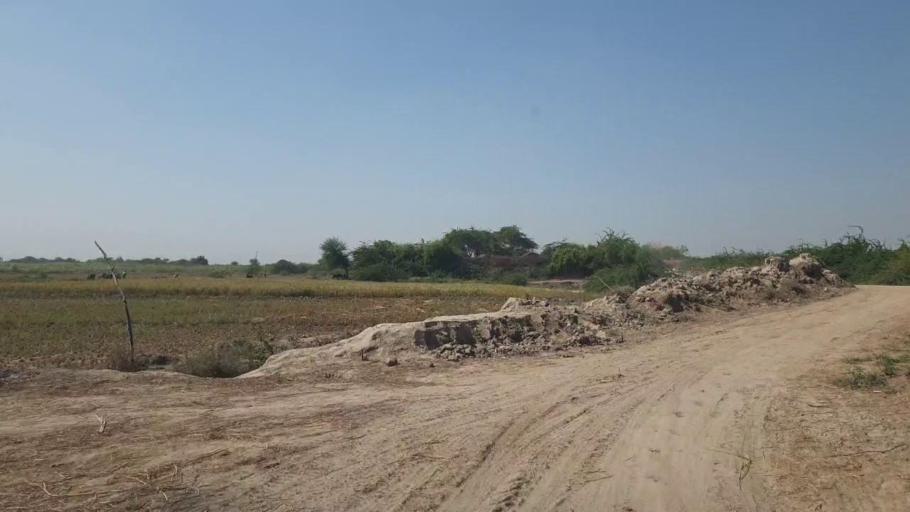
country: PK
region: Sindh
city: Talhar
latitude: 24.8060
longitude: 68.7958
